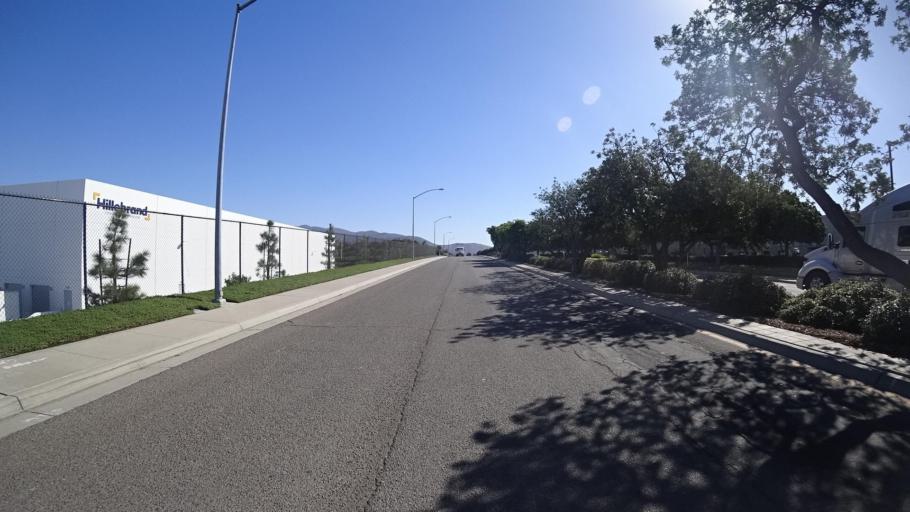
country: MX
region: Baja California
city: Tijuana
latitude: 32.5603
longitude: -116.9379
